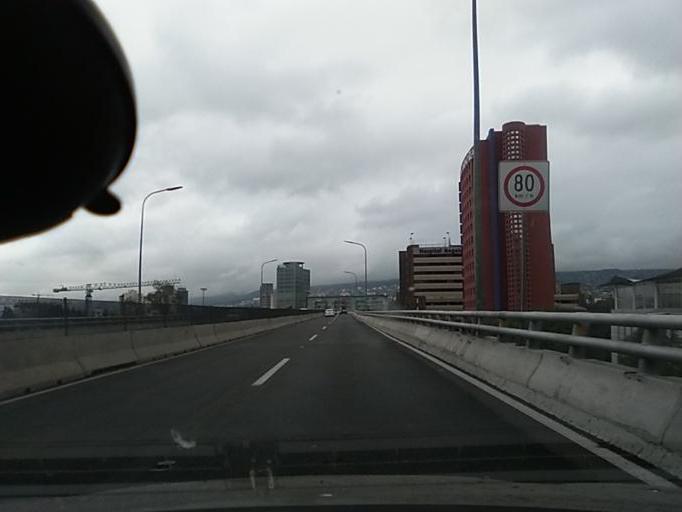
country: MX
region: Mexico City
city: Magdalena Contreras
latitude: 19.3158
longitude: -99.2210
